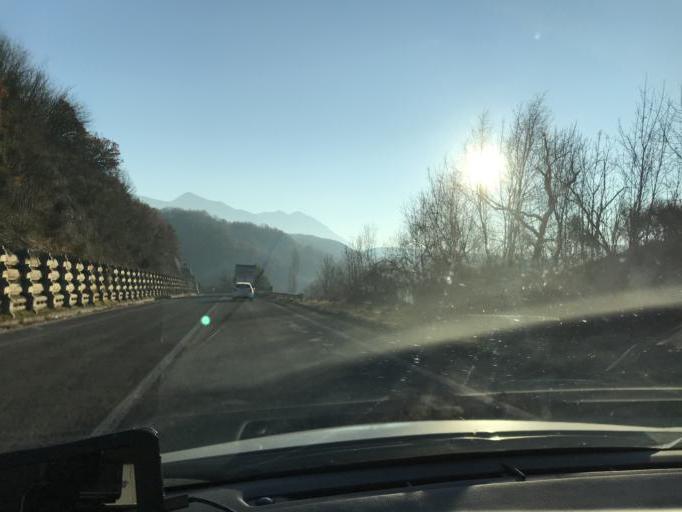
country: IT
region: Latium
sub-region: Provincia di Rieti
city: Borgorose
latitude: 42.1950
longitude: 13.2340
